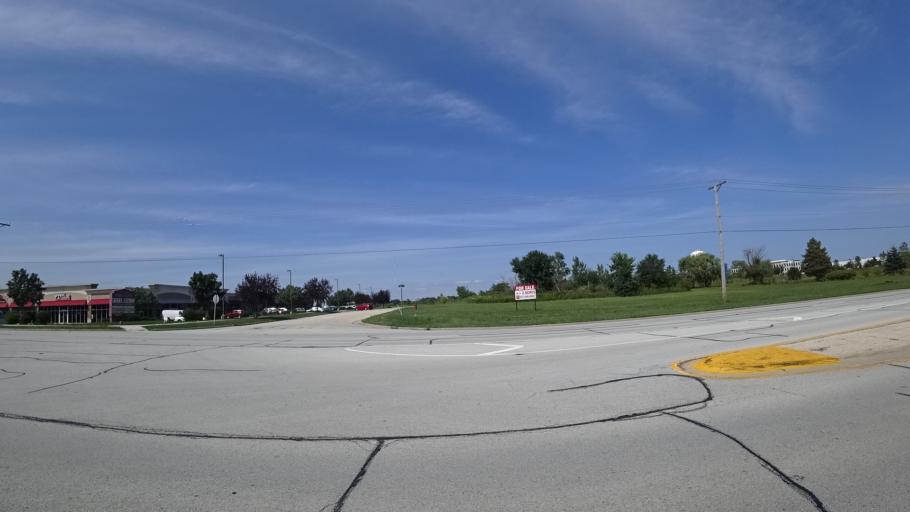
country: US
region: Illinois
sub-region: Cook County
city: Orland Hills
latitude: 41.5431
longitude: -87.8461
